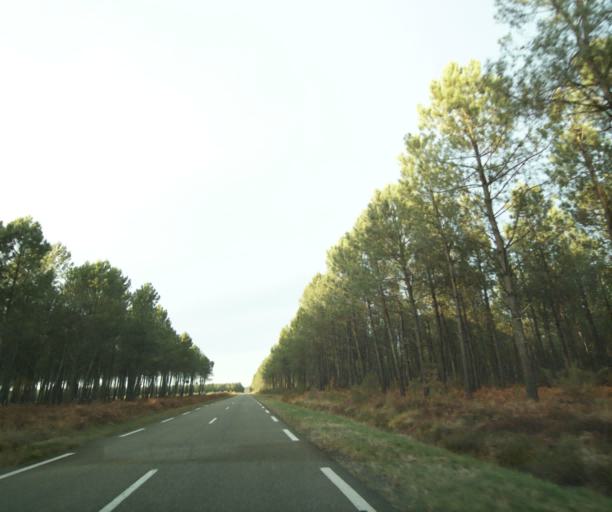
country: FR
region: Aquitaine
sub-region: Departement des Landes
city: Gabarret
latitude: 44.1569
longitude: -0.1317
